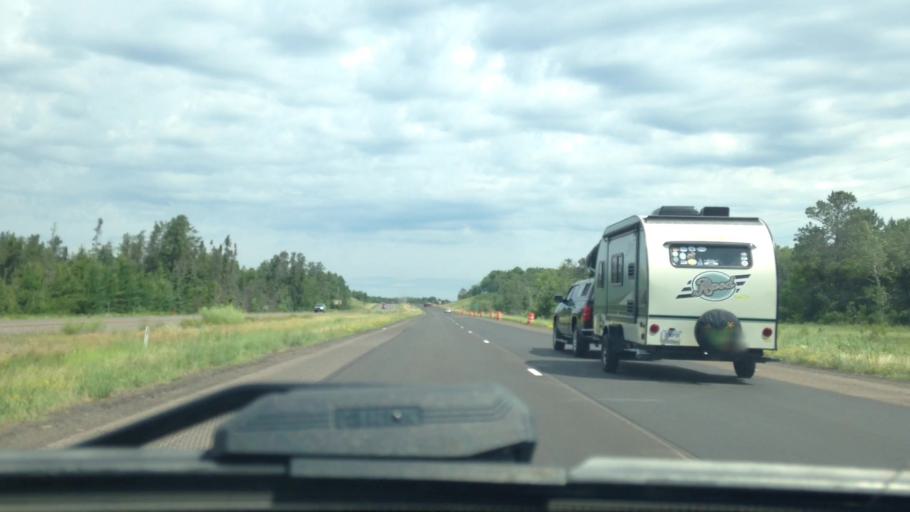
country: US
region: Wisconsin
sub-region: Washburn County
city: Spooner
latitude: 46.1678
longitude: -91.8061
